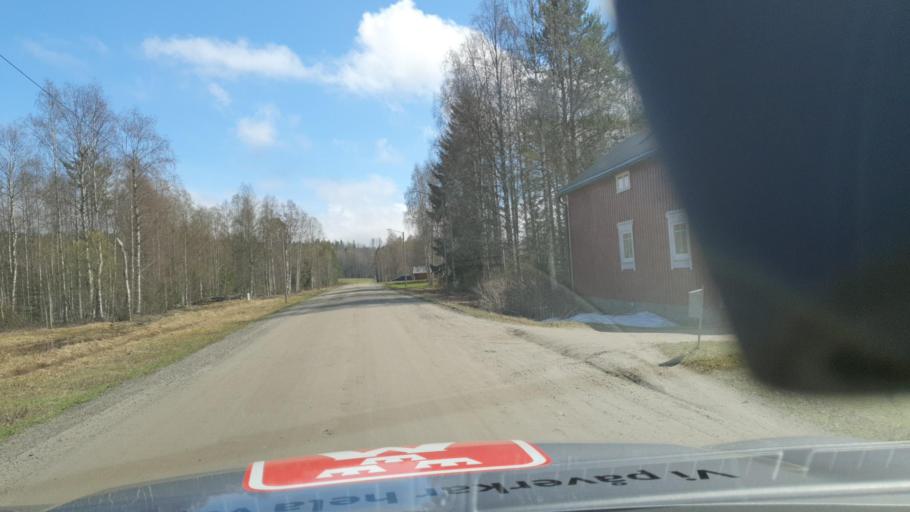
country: SE
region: Vaesterbotten
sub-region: Bjurholms Kommun
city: Bjurholm
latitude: 63.6972
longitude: 18.9509
